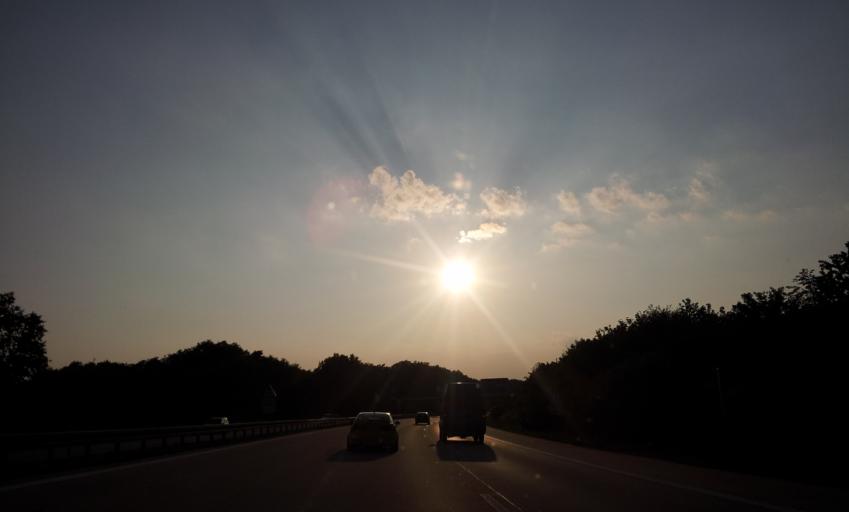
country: DE
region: Brandenburg
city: Wildau
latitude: 52.3116
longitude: 13.6074
